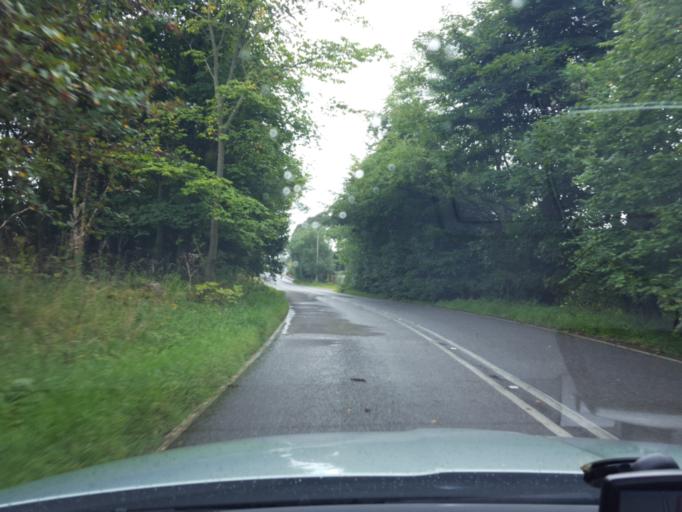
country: GB
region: Scotland
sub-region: Aberdeenshire
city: Laurencekirk
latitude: 56.8769
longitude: -2.4067
